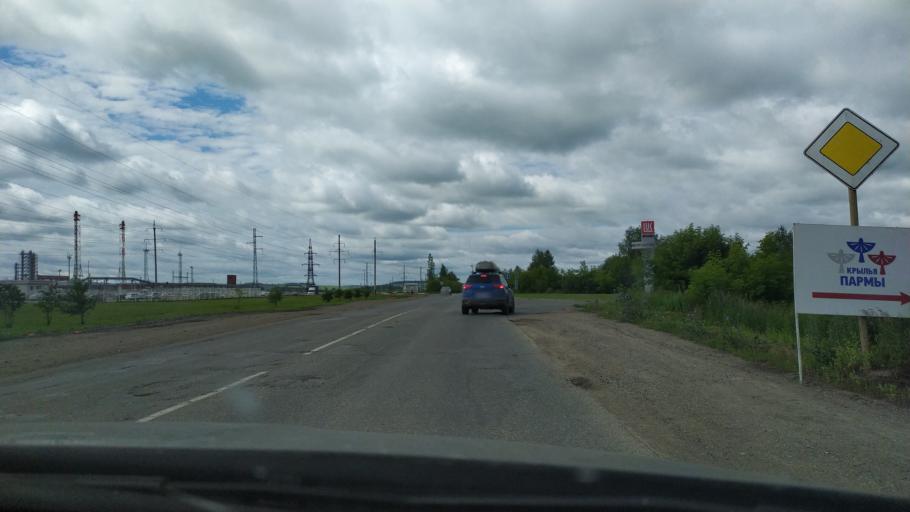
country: RU
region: Perm
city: Kondratovo
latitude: 57.9276
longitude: 56.1164
